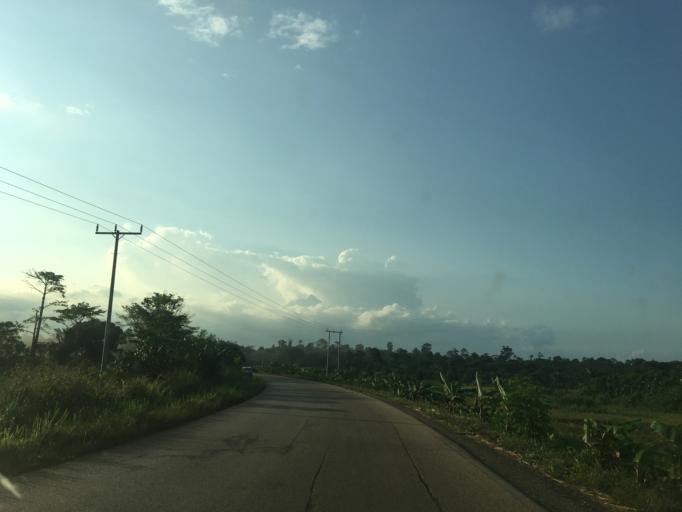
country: GH
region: Western
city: Bibiani
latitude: 6.5733
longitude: -2.3722
